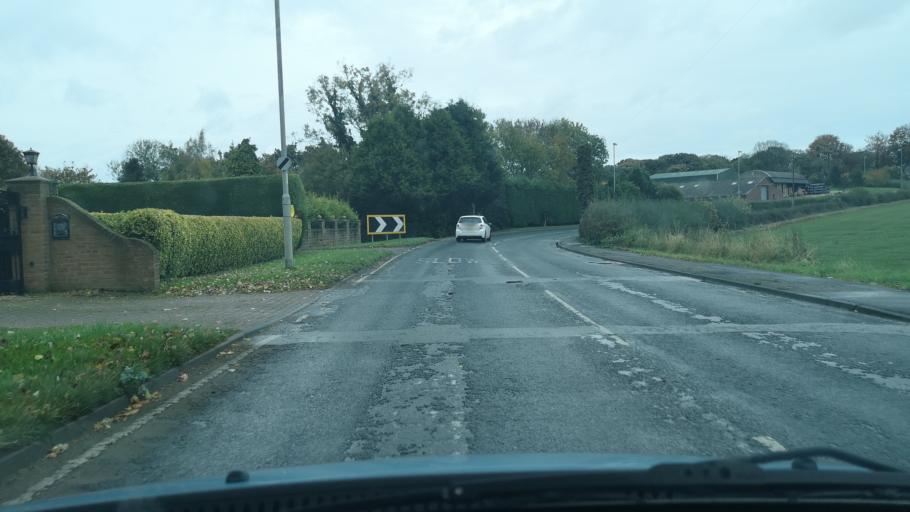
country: GB
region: England
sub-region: City and Borough of Wakefield
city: Hemsworth
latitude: 53.6201
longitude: -1.3464
